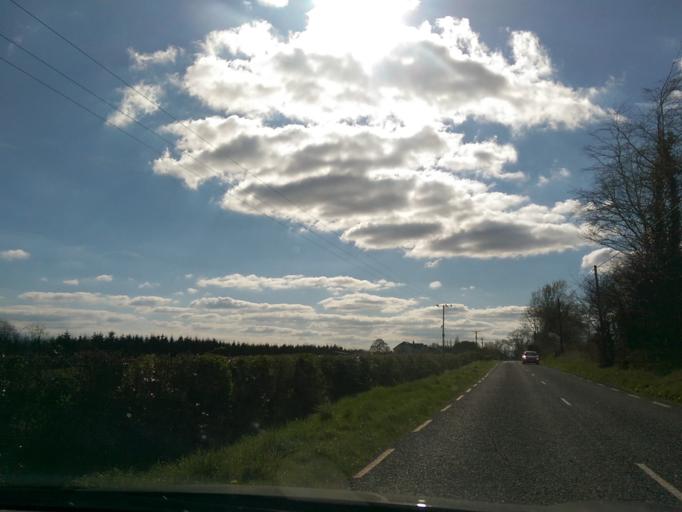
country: IE
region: Leinster
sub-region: Uibh Fhaili
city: Birr
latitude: 53.1040
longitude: -7.7935
